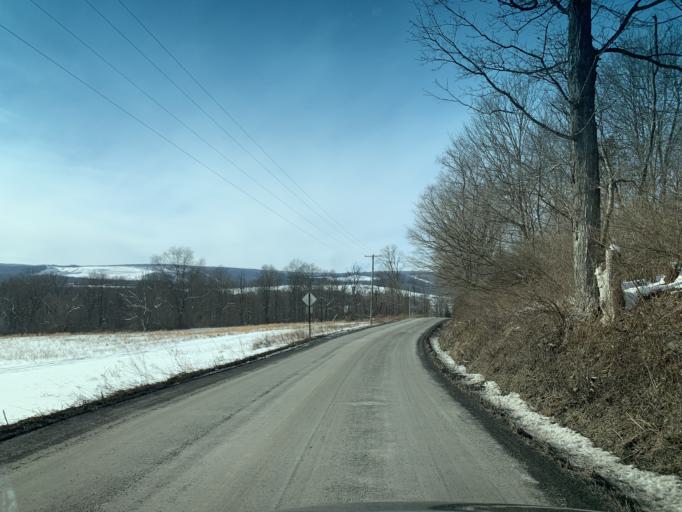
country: US
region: Maryland
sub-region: Allegany County
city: Frostburg
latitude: 39.6202
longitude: -78.9335
